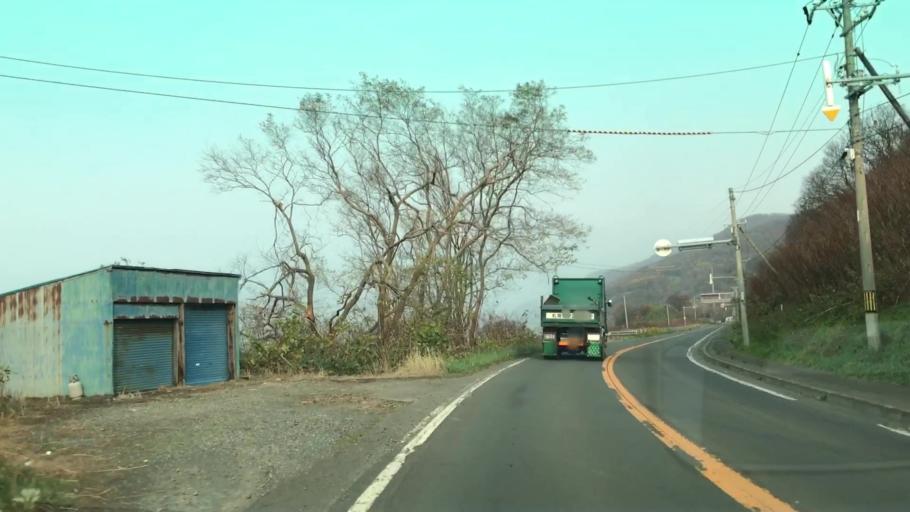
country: JP
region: Hokkaido
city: Ishikari
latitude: 43.4151
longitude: 141.4305
